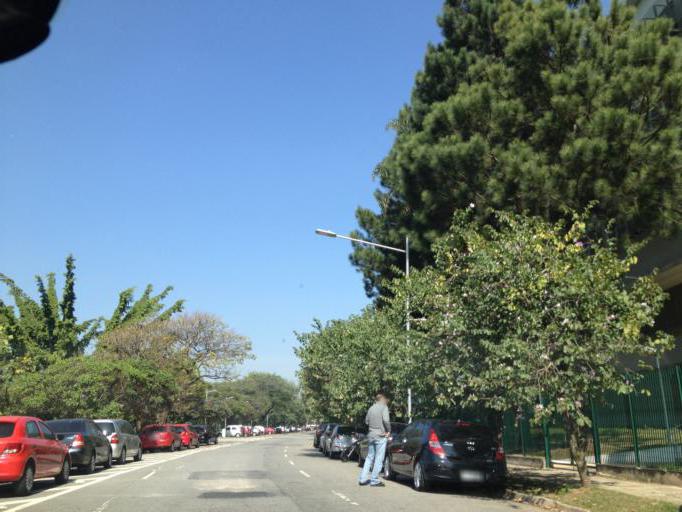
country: BR
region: Sao Paulo
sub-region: Sao Paulo
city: Sao Paulo
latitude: -23.5611
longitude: -46.7131
